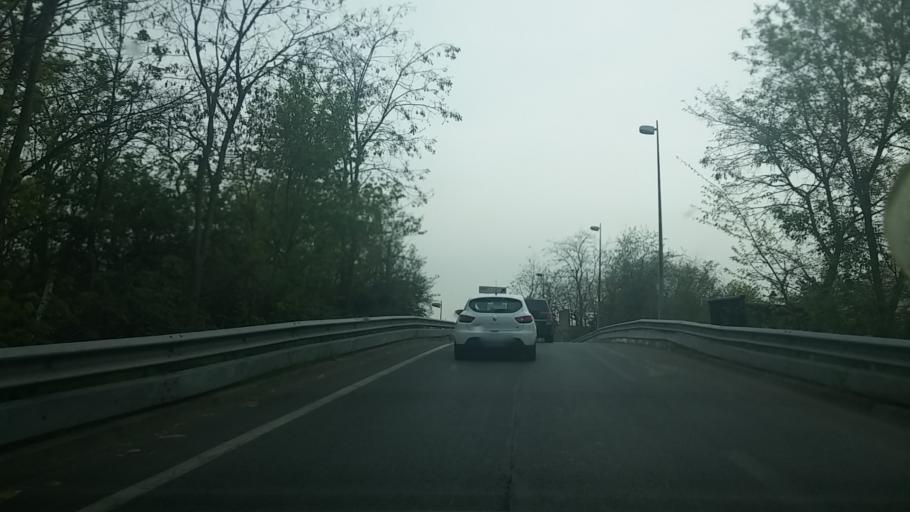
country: FR
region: Ile-de-France
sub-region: Departement du Val-de-Marne
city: Maisons-Alfort
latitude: 48.8024
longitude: 2.4459
